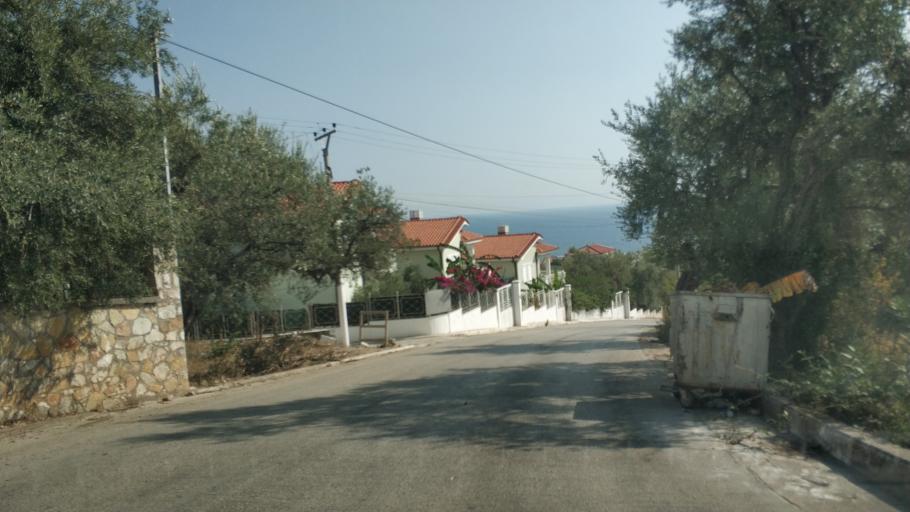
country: AL
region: Vlore
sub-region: Rrethi i Vlores
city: Vranisht
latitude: 40.1481
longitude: 19.6341
